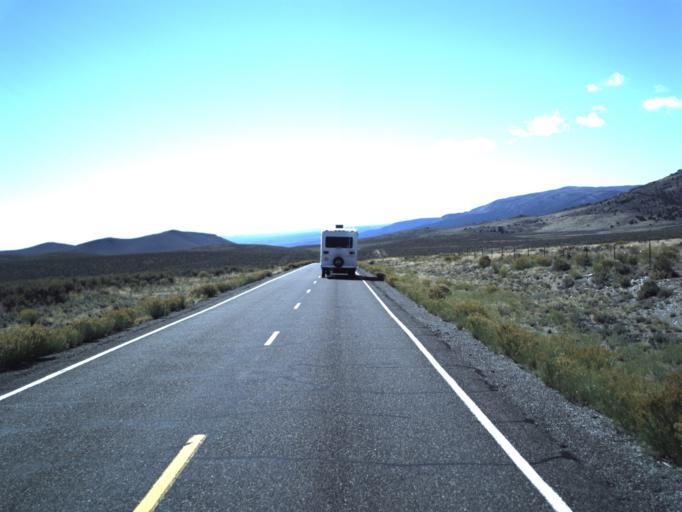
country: US
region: Utah
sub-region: Piute County
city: Junction
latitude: 38.3275
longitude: -111.9599
